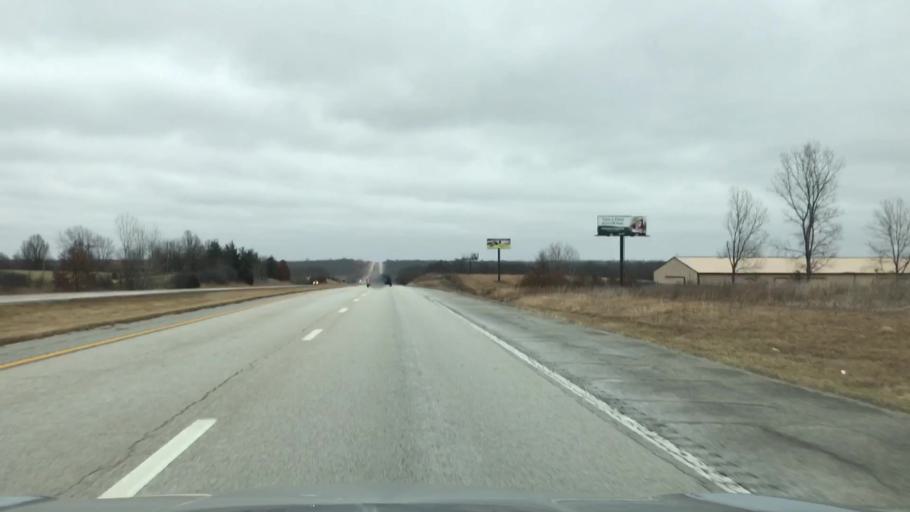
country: US
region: Missouri
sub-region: Clinton County
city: Cameron
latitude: 39.7520
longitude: -94.1852
